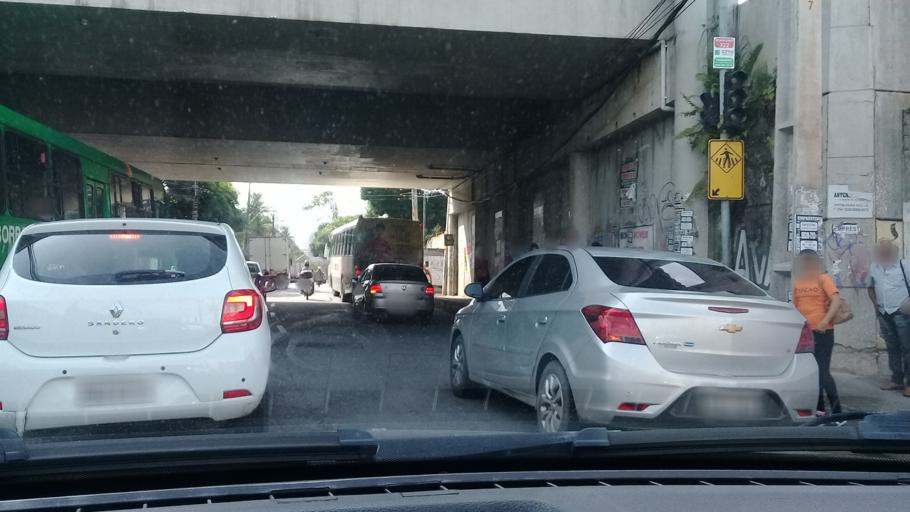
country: BR
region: Pernambuco
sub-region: Recife
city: Recife
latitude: -8.1345
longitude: -34.9150
